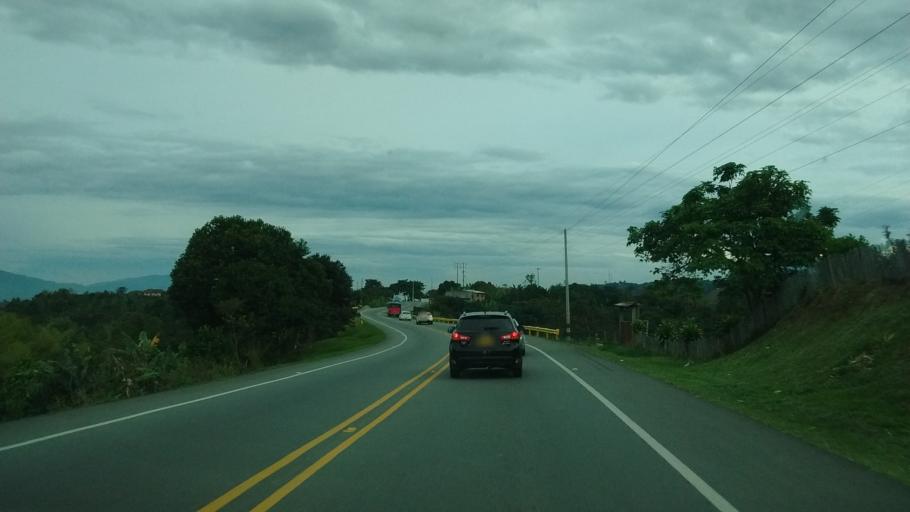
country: CO
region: Cauca
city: Morales
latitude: 2.7620
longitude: -76.5535
